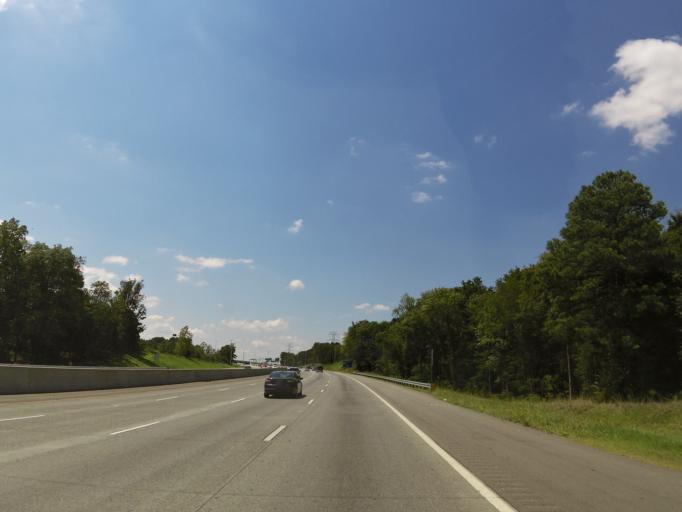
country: US
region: North Carolina
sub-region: Cabarrus County
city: Kannapolis
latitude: 35.4387
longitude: -80.6482
